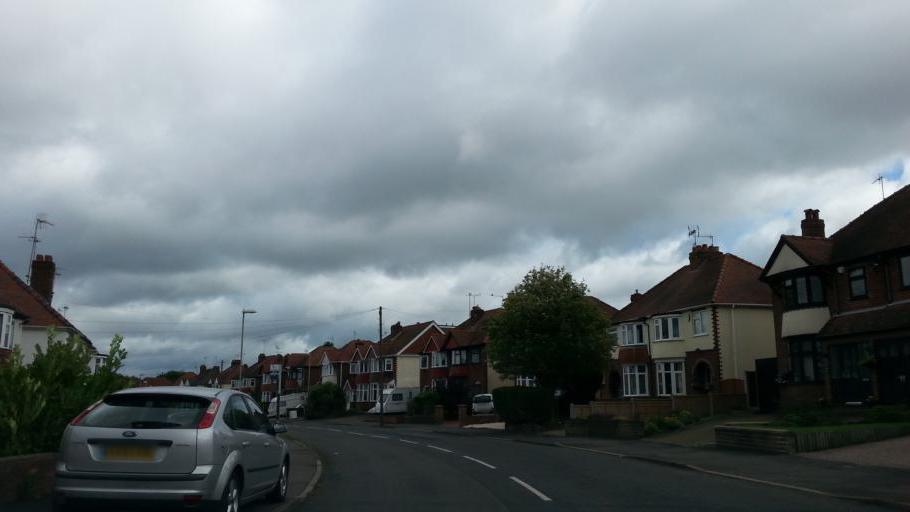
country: GB
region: England
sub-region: Dudley
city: Halesowen
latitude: 52.4523
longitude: -2.0705
